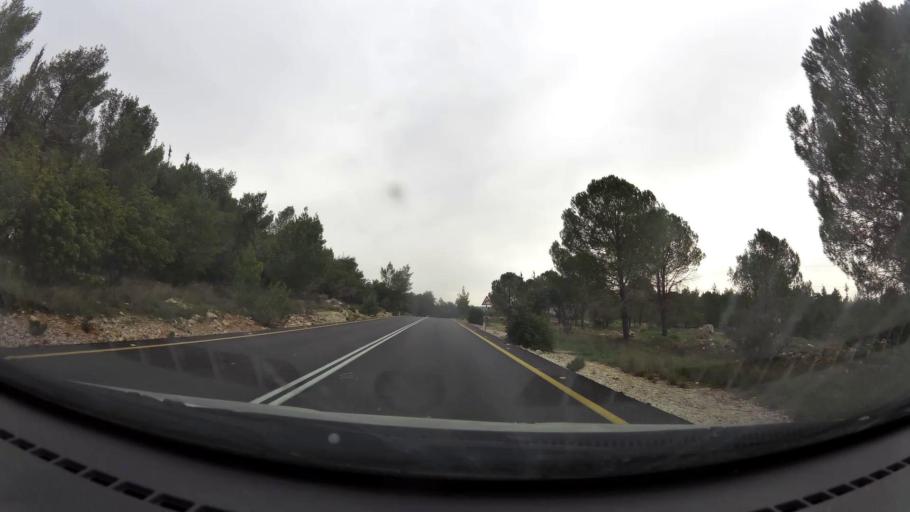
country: PS
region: West Bank
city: Surif
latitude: 31.6749
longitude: 35.0450
